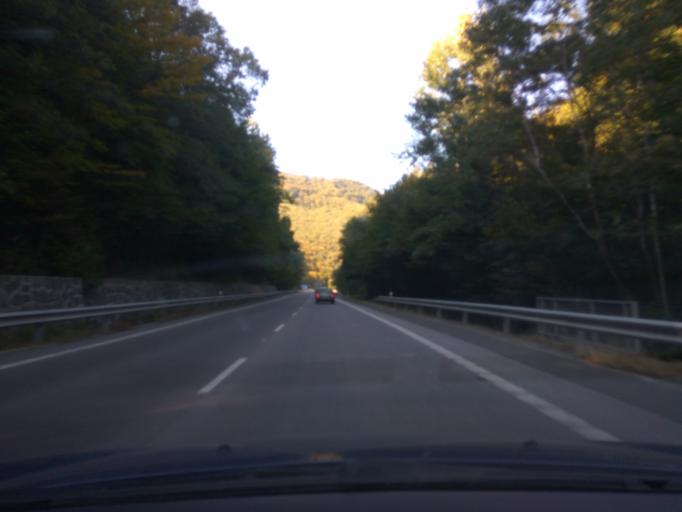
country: SK
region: Banskobystricky
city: Ziar nad Hronom
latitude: 48.6347
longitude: 18.9020
